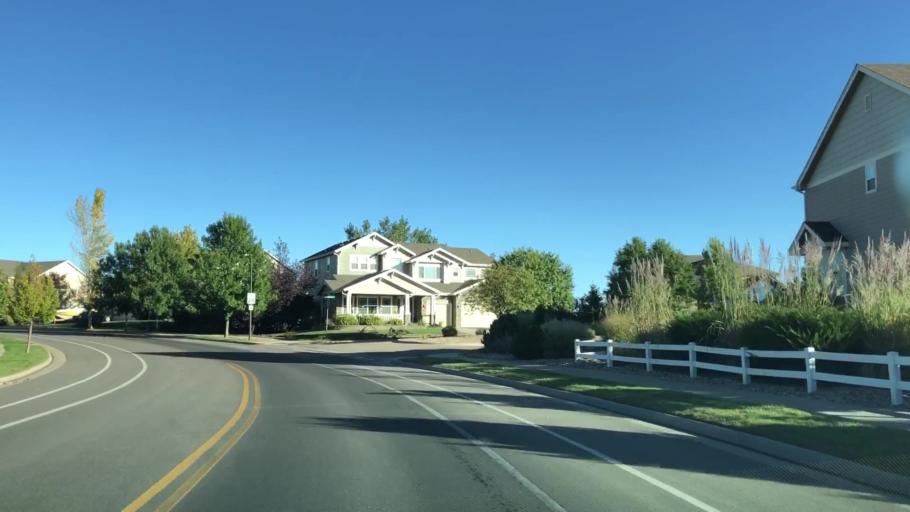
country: US
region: Colorado
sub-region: Larimer County
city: Loveland
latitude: 40.4604
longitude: -105.0324
